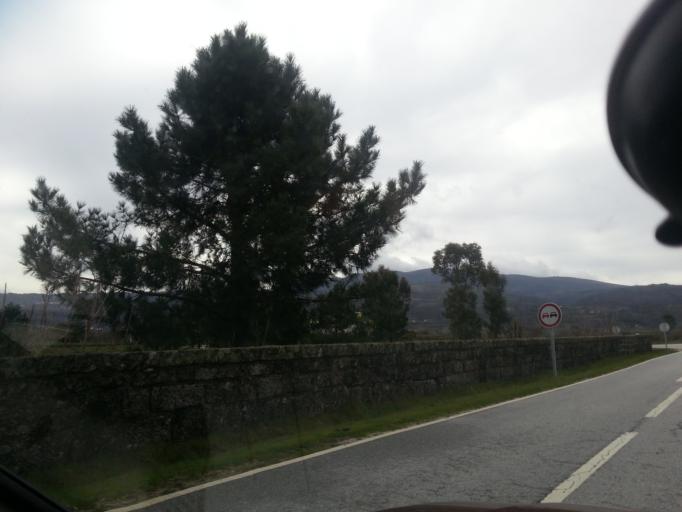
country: PT
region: Guarda
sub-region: Fornos de Algodres
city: Fornos de Algodres
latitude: 40.5392
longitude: -7.5698
